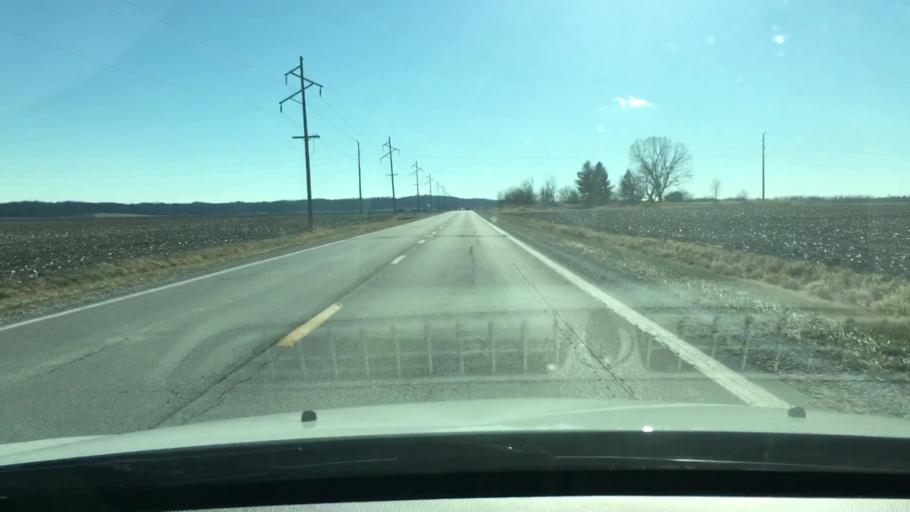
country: US
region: Illinois
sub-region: Morgan County
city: Meredosia
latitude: 39.8667
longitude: -90.5054
